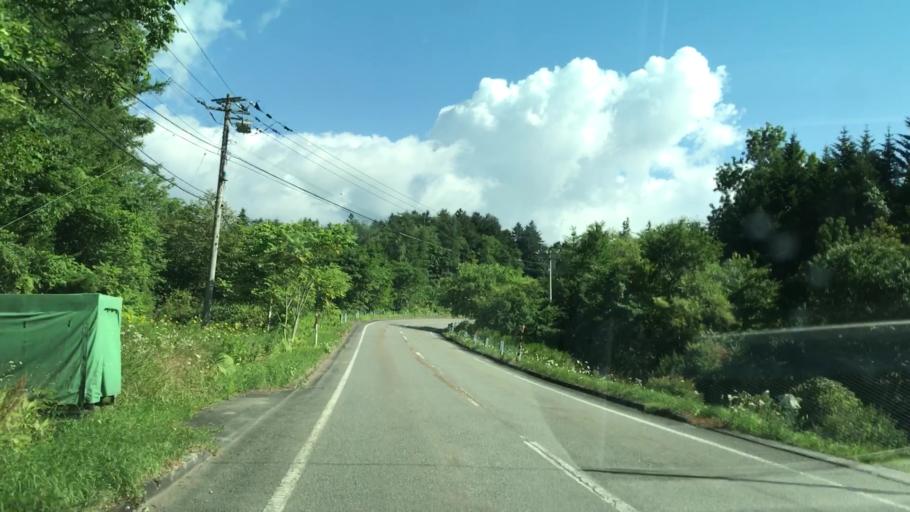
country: JP
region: Hokkaido
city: Shimo-furano
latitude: 42.8641
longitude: 142.4402
